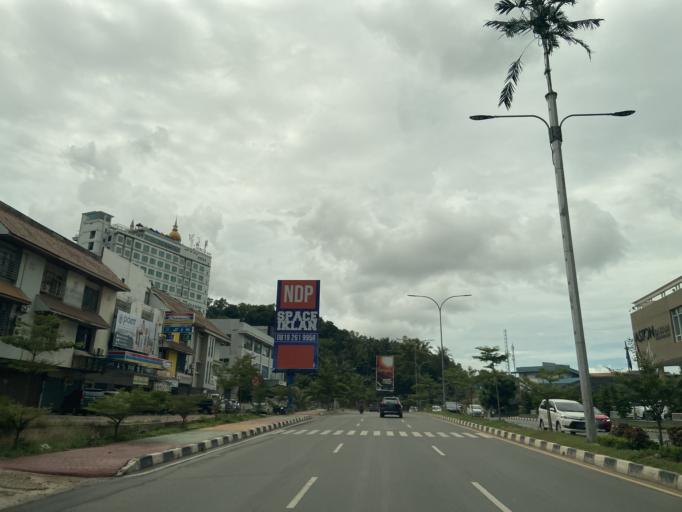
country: SG
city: Singapore
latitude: 1.1433
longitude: 104.0204
